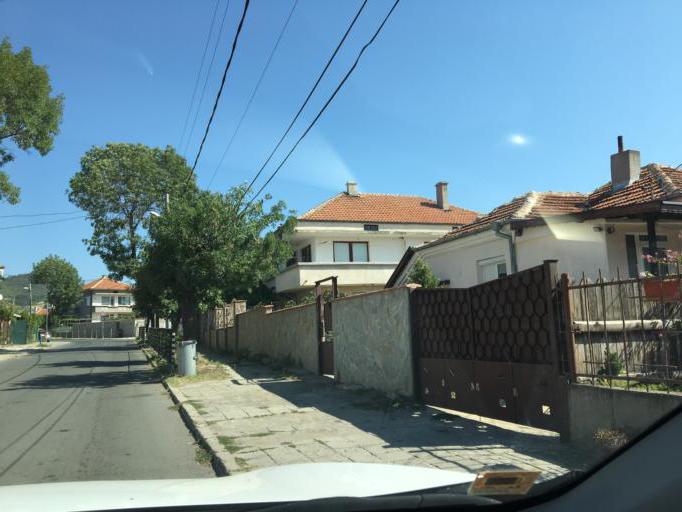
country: BG
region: Burgas
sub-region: Obshtina Kameno
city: Kameno
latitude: 42.6253
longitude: 27.3958
